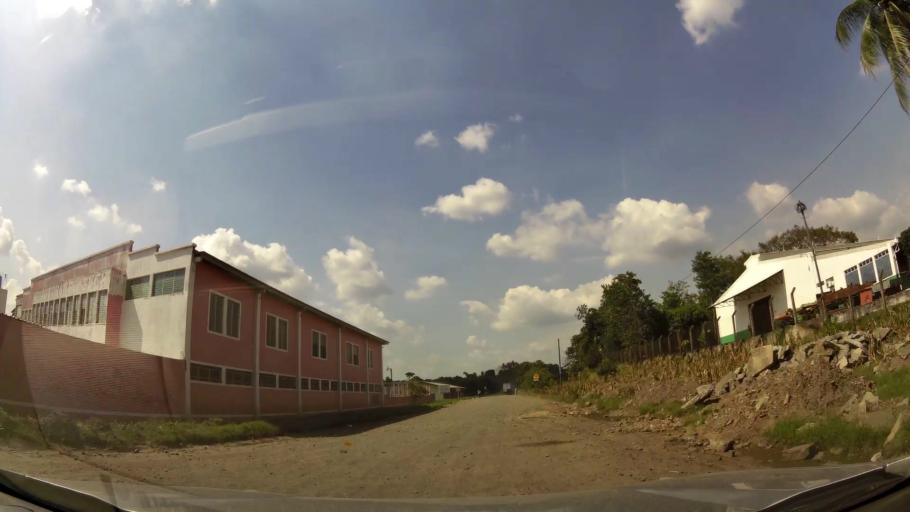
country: GT
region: Suchitepeque
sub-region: Municipio de Cuyotenango
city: Cuyotenango
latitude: 14.5438
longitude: -91.5681
